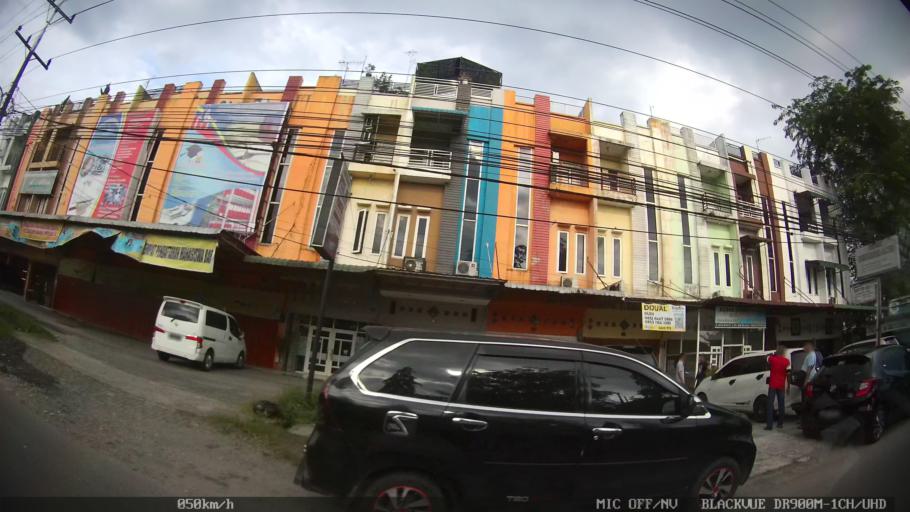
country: ID
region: North Sumatra
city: Sunggal
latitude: 3.5369
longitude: 98.6223
